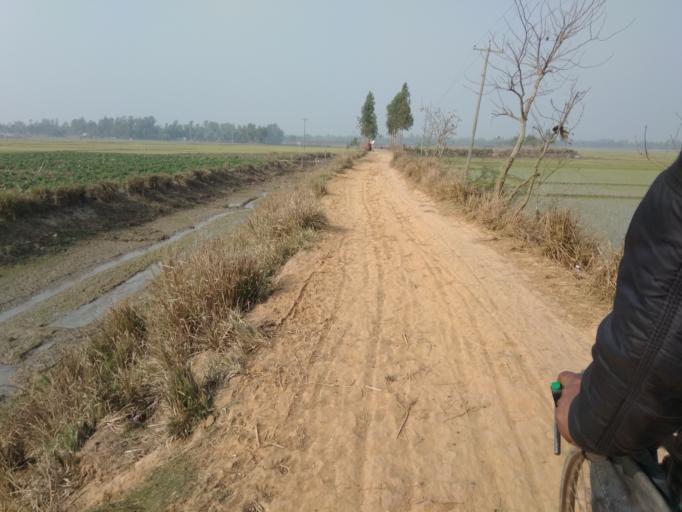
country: BD
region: Rajshahi
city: Ishurdi
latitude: 24.4670
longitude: 89.2670
